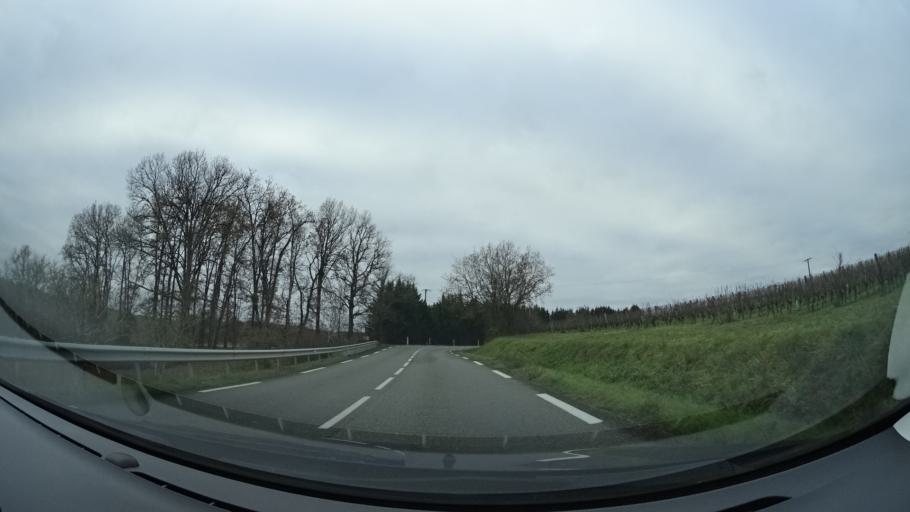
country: FR
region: Aquitaine
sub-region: Departement du Lot-et-Garonne
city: Damazan
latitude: 44.2754
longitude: 0.2602
